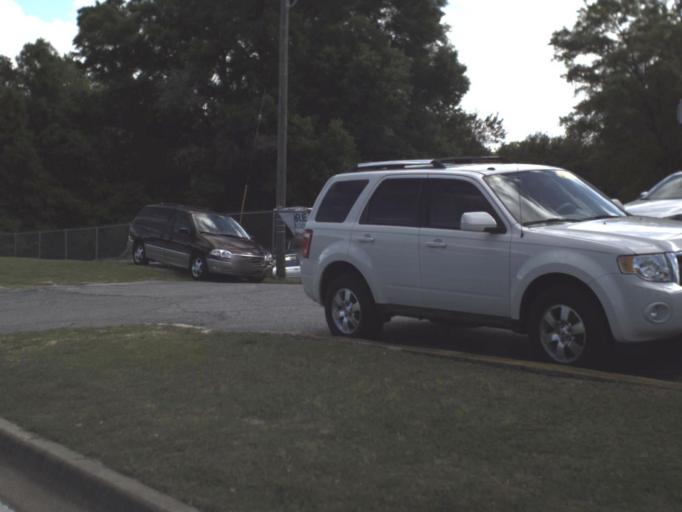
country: US
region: Florida
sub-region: Escambia County
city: West Pensacola
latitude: 30.4104
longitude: -87.2763
